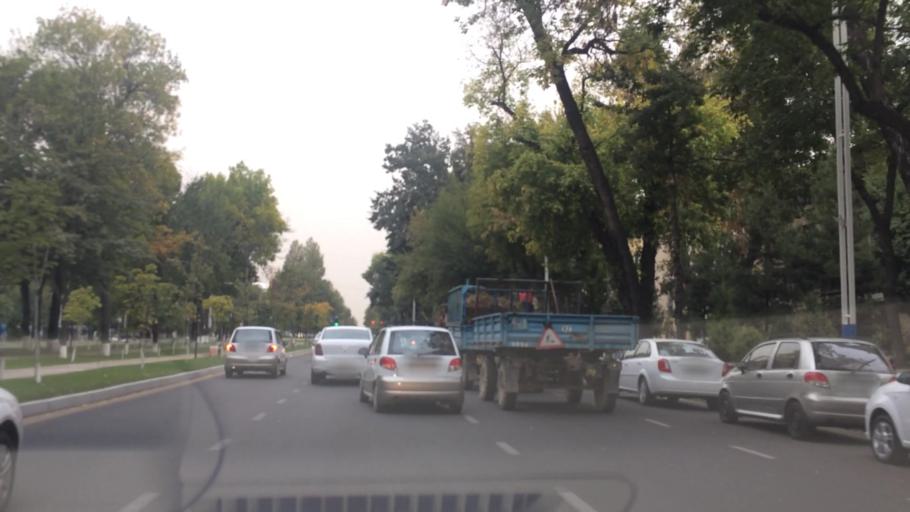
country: UZ
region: Toshkent Shahri
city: Tashkent
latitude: 41.3082
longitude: 69.2909
